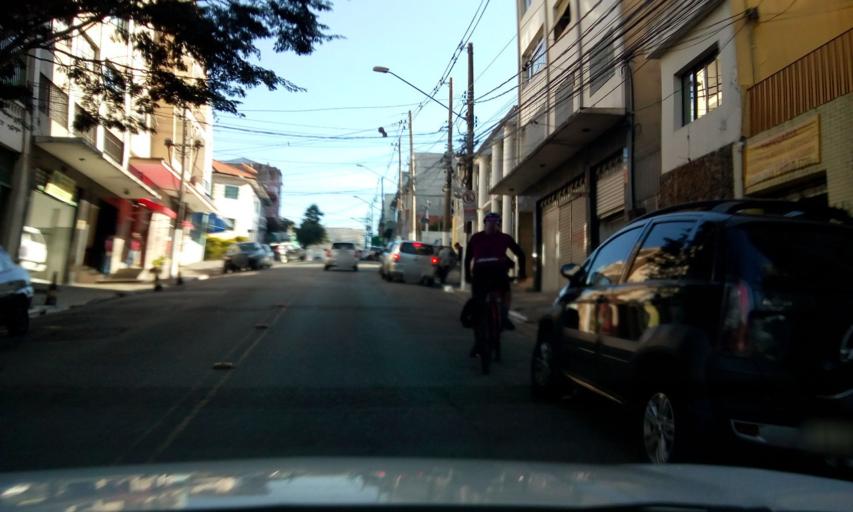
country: BR
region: Sao Paulo
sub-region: Sao Paulo
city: Sao Paulo
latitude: -23.5817
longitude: -46.6361
